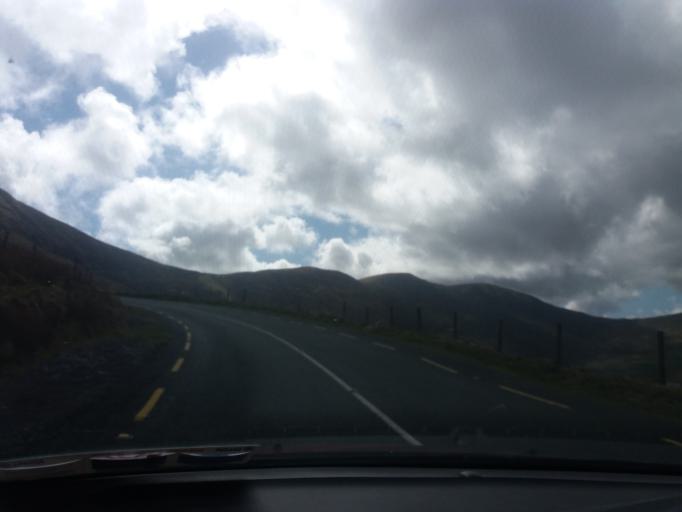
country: IE
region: Munster
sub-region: Ciarrai
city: Dingle
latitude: 52.1899
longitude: -10.1908
